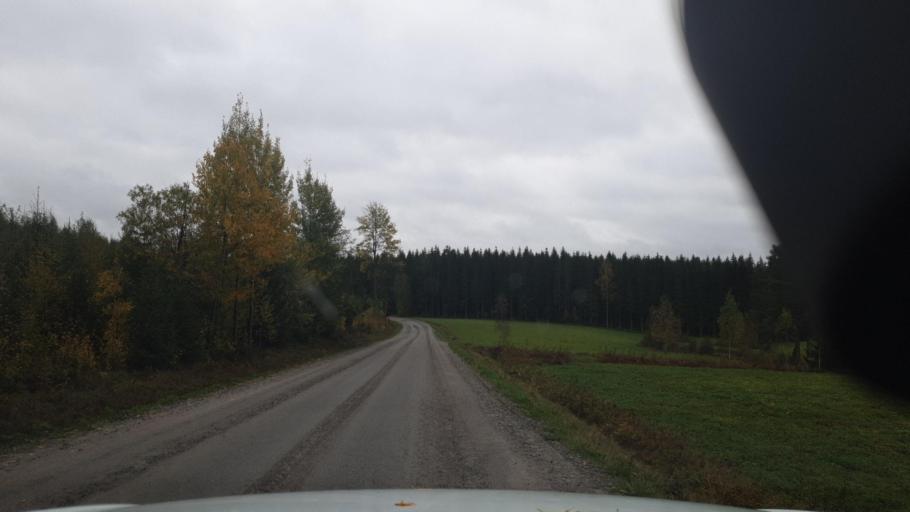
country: SE
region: Vaermland
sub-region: Karlstads Kommun
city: Edsvalla
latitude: 59.4904
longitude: 13.0322
